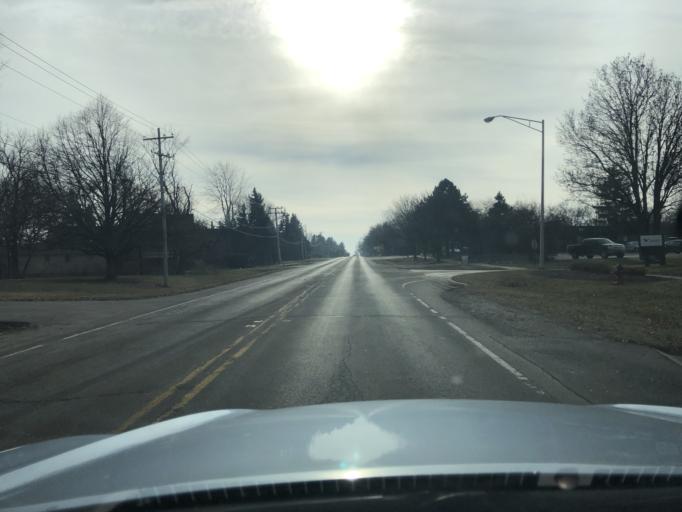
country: US
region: Illinois
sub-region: DuPage County
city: Itasca
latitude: 41.9820
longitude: -88.0047
